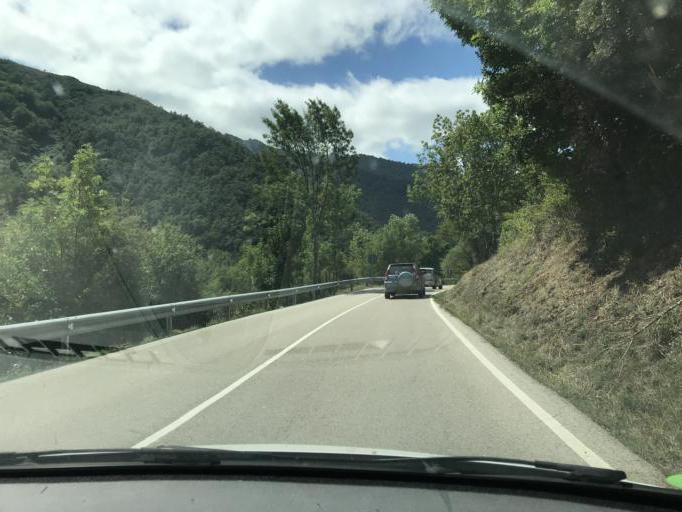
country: ES
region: Cantabria
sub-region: Provincia de Cantabria
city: Cabezon de Liebana
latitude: 43.0742
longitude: -4.5270
